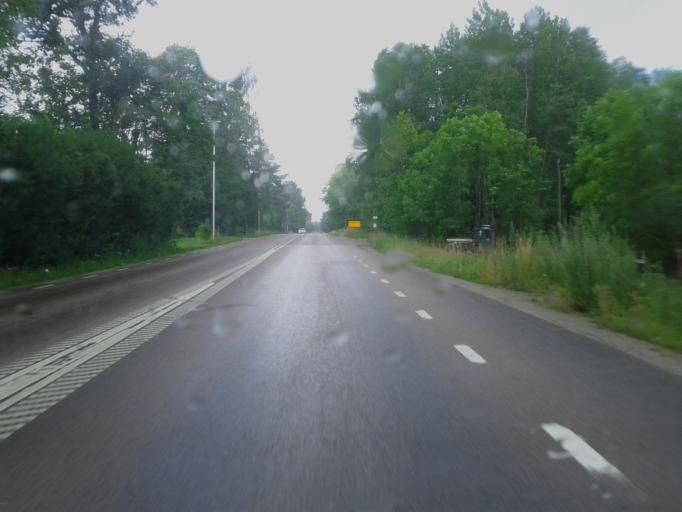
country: SE
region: Vaestmanland
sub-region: Sala Kommun
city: Sala
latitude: 59.8905
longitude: 16.5647
